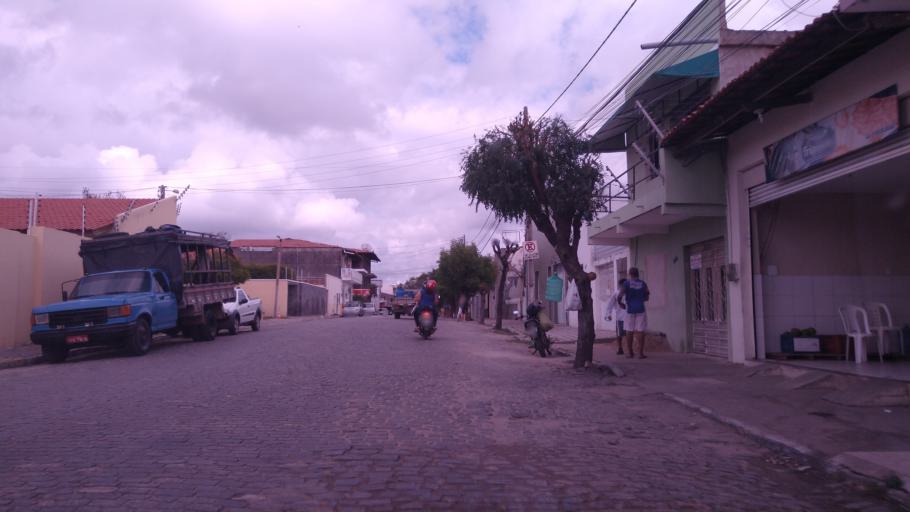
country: BR
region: Ceara
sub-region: Quixada
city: Quixada
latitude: -4.9670
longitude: -39.0176
